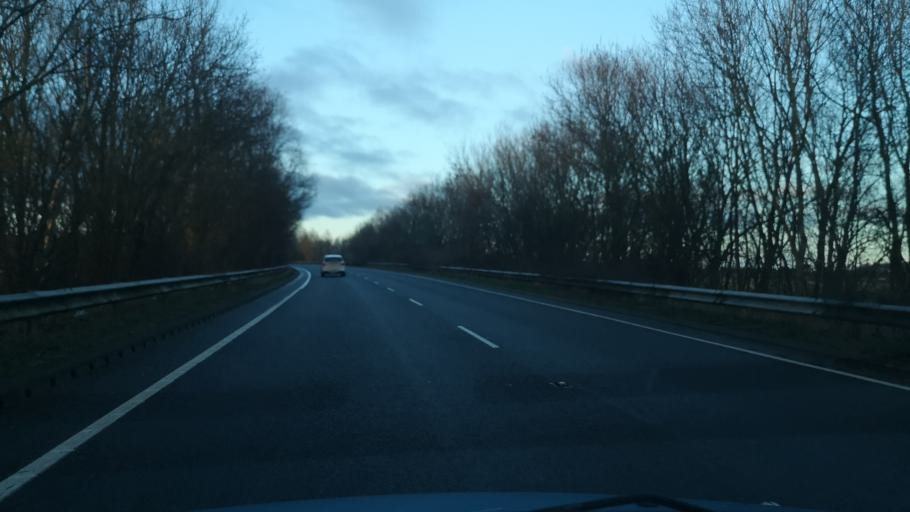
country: GB
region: England
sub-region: City and Borough of Wakefield
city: Hemsworth
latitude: 53.6113
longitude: -1.3363
